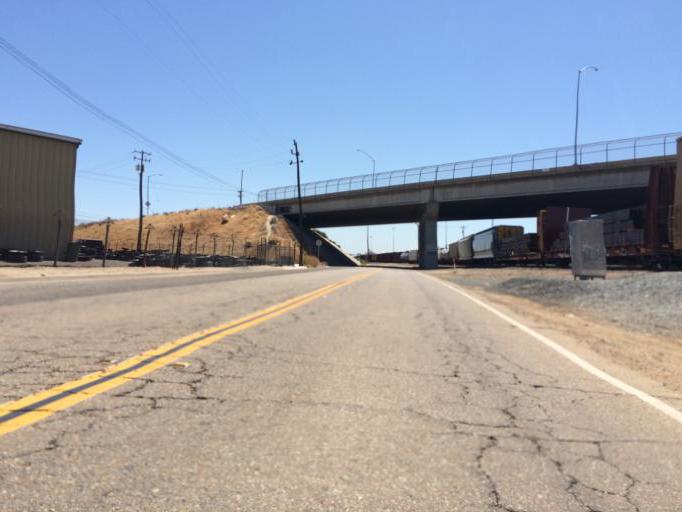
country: US
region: California
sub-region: Fresno County
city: Fresno
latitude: 36.7075
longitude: -119.7655
